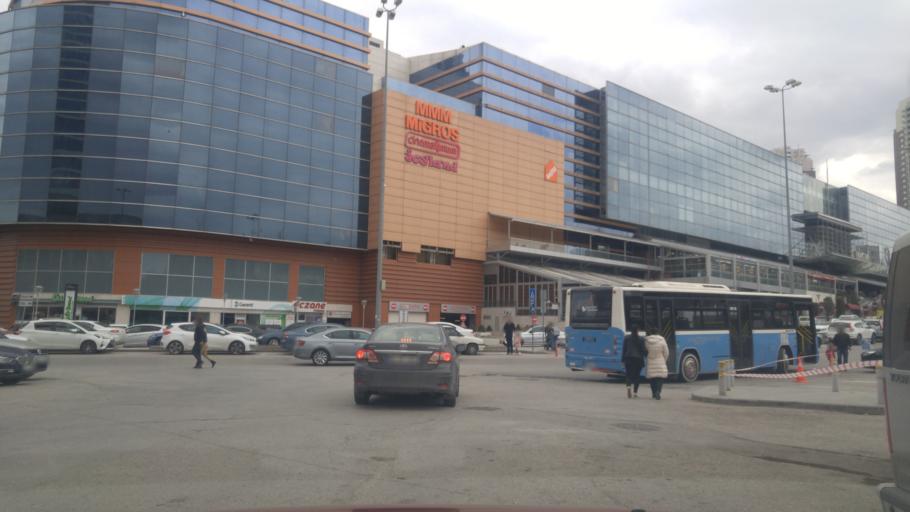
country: TR
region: Ankara
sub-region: Goelbasi
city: Golbasi
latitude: 39.8495
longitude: 32.8341
